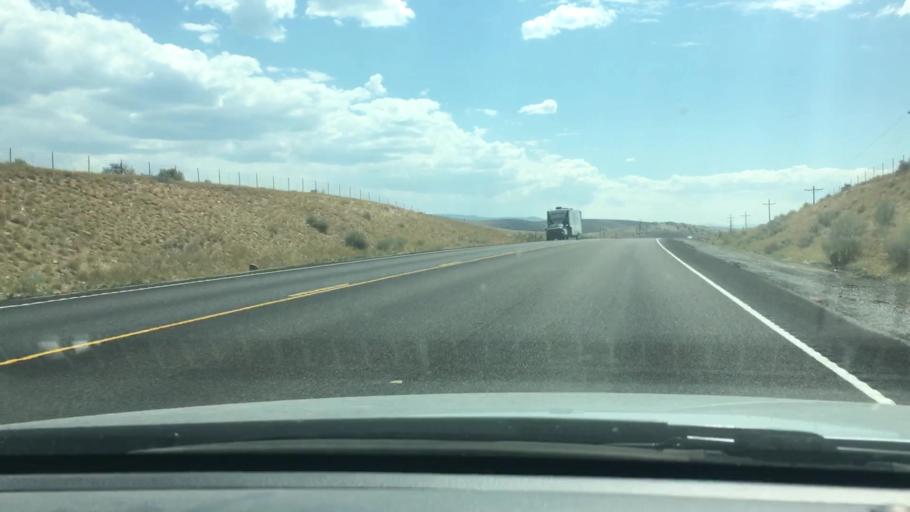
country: US
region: Utah
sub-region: Utah County
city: Woodland Hills
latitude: 39.8511
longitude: -111.5190
